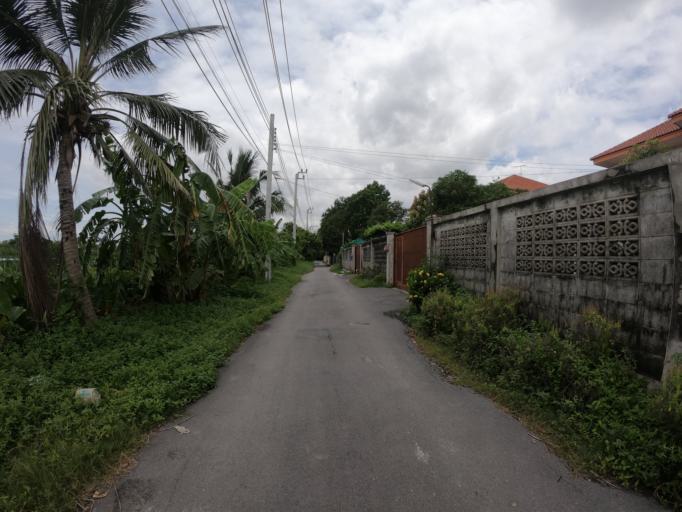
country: TH
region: Bangkok
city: Lat Phrao
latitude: 13.8243
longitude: 100.6238
